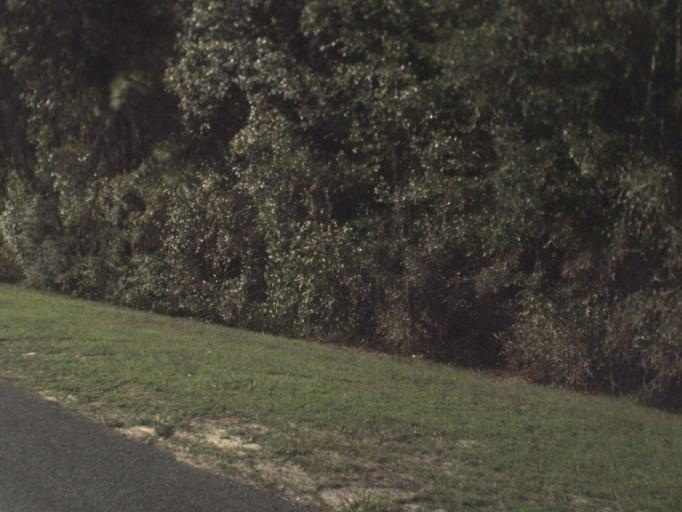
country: US
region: Florida
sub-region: Bay County
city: Youngstown
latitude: 30.4275
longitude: -85.5683
